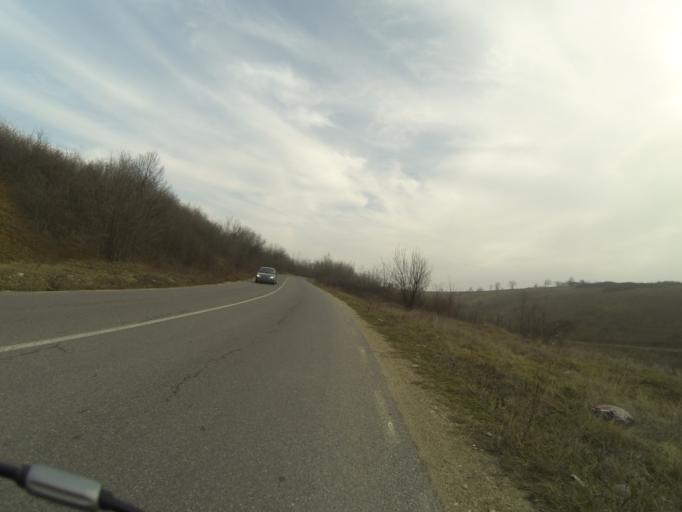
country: RO
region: Mehedinti
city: Vanju-Mare
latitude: 44.4116
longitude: 22.8835
